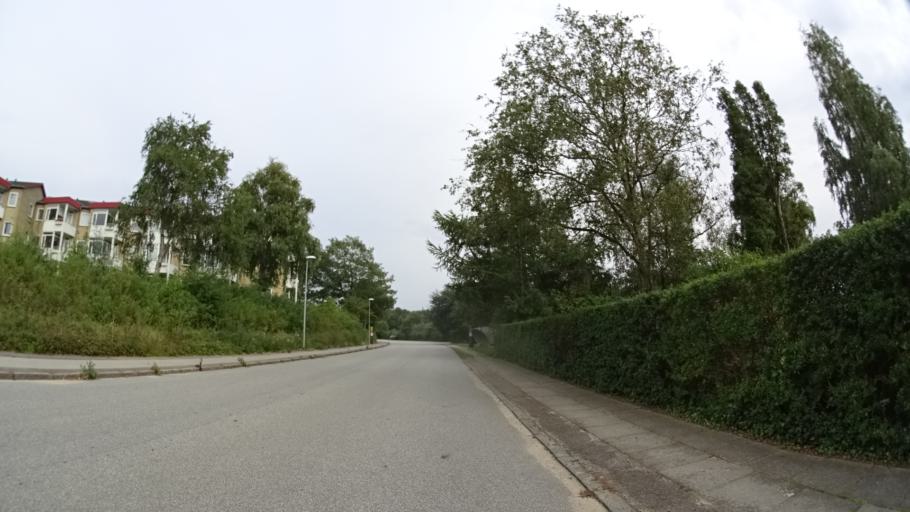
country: DK
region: Central Jutland
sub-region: Arhus Kommune
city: Stavtrup
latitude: 56.1496
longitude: 10.1285
